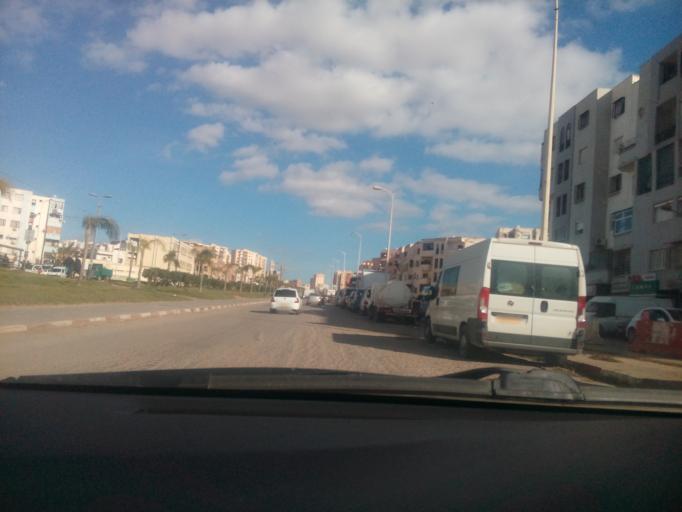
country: DZ
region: Oran
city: Bir el Djir
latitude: 35.6951
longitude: -0.5734
